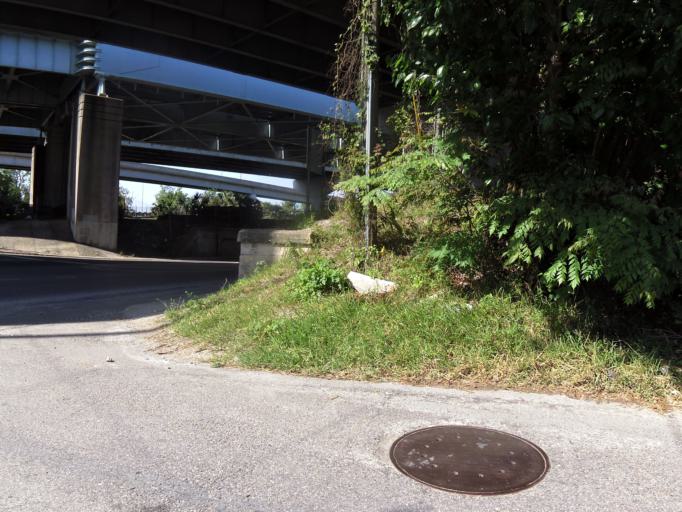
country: US
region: Florida
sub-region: Duval County
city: Jacksonville
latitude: 30.3283
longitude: -81.6767
